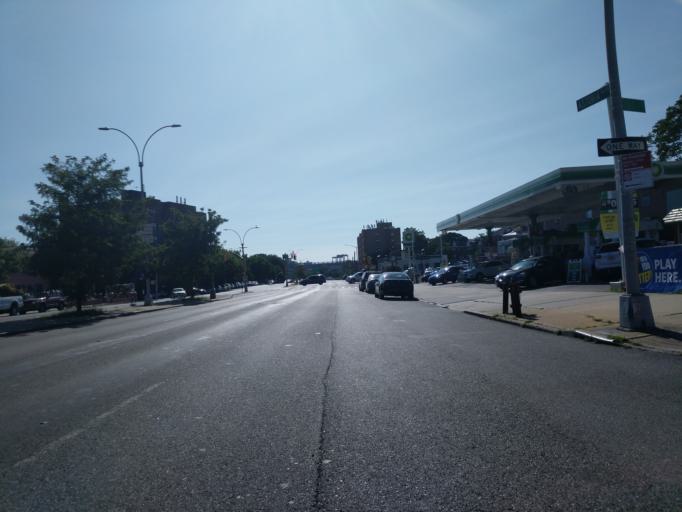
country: US
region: New York
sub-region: Queens County
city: Borough of Queens
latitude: 40.7607
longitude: -73.8624
